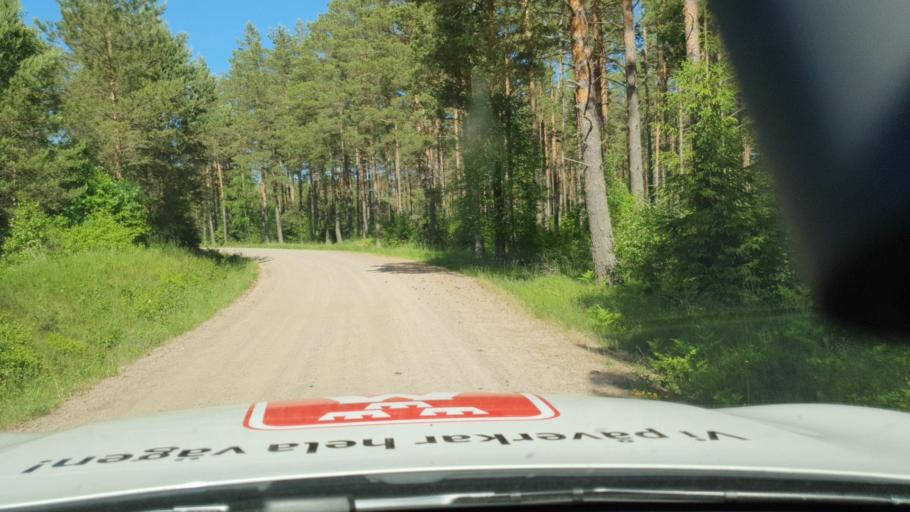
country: SE
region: Vaestra Goetaland
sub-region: Skovde Kommun
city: Skultorp
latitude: 58.3087
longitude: 13.8451
